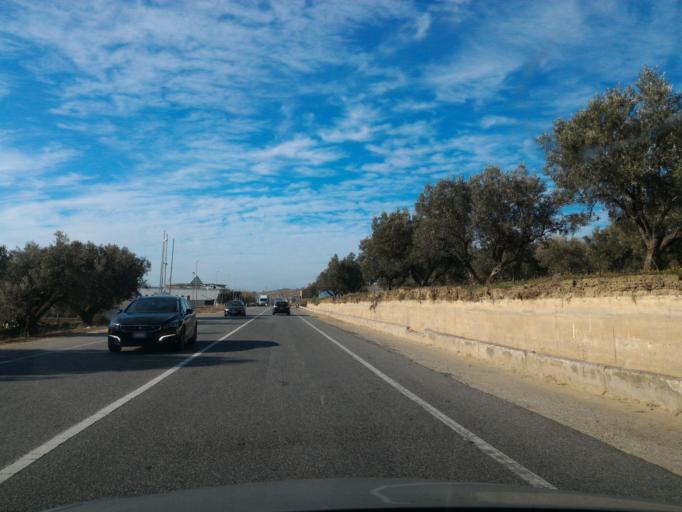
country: IT
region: Calabria
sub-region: Provincia di Catanzaro
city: Cropani Marina
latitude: 38.9265
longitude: 16.8213
